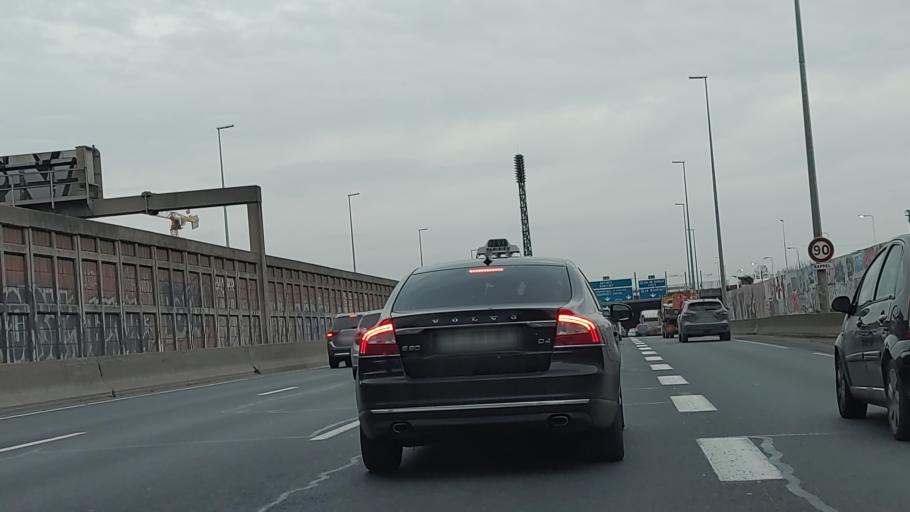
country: FR
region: Ile-de-France
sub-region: Departement de Seine-Saint-Denis
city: La Courneuve
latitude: 48.9270
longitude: 2.3922
